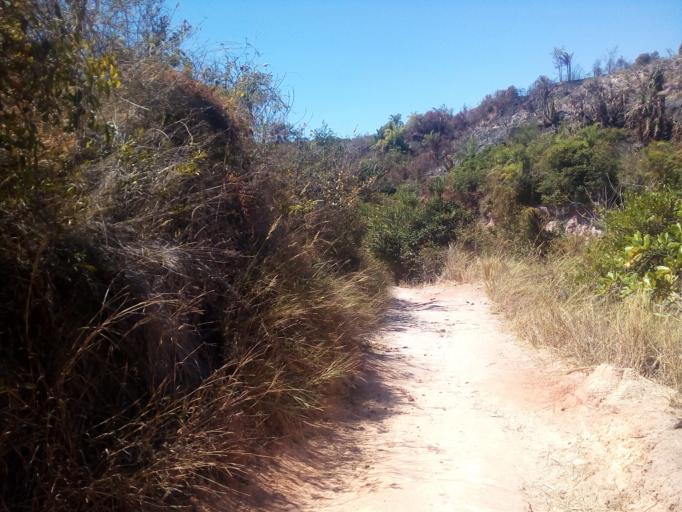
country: MG
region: Boeny
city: Mahajanga
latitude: -15.6330
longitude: 46.3505
